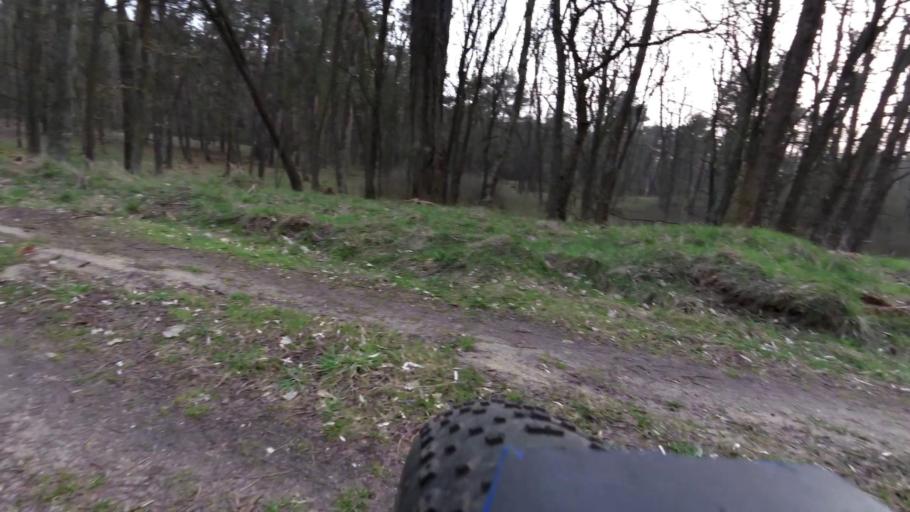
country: DE
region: Brandenburg
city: Ziltendorf
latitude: 52.2794
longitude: 14.6769
